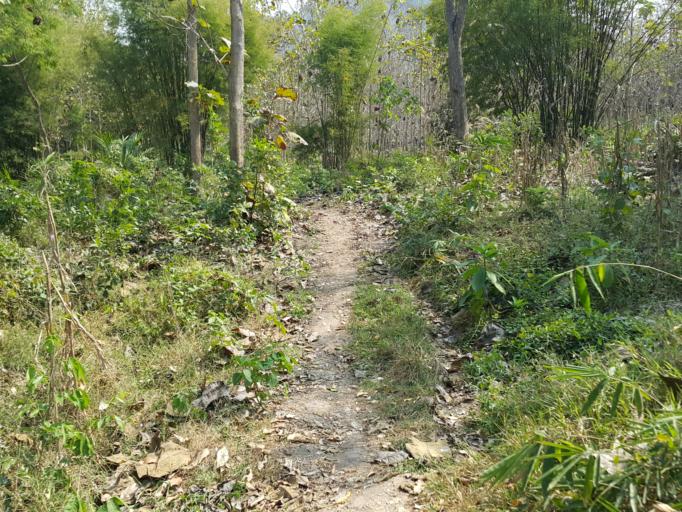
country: TH
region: Sukhothai
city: Thung Saliam
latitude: 17.3253
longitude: 99.5019
